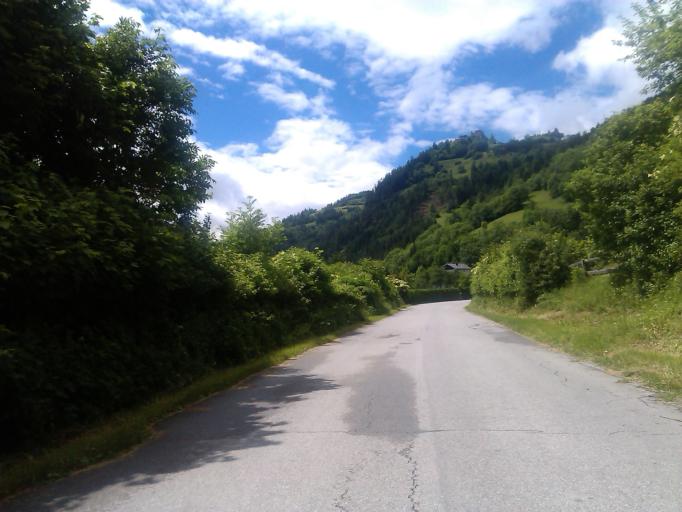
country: AT
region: Tyrol
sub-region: Politischer Bezirk Landeck
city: Prutz
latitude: 47.0870
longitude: 10.6620
